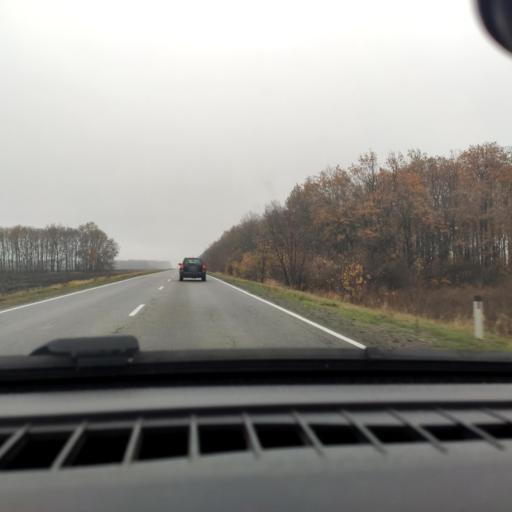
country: RU
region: Voronezj
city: Shilovo
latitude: 51.4184
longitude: 39.0060
